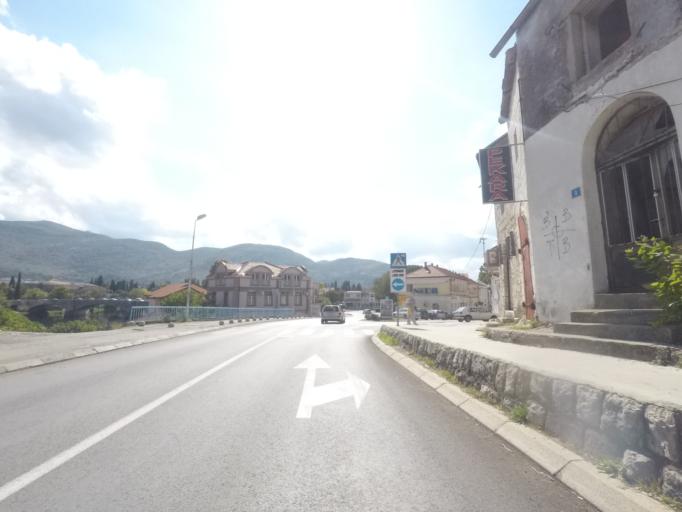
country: BA
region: Republika Srpska
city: Trebinje
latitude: 42.7130
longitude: 18.3465
